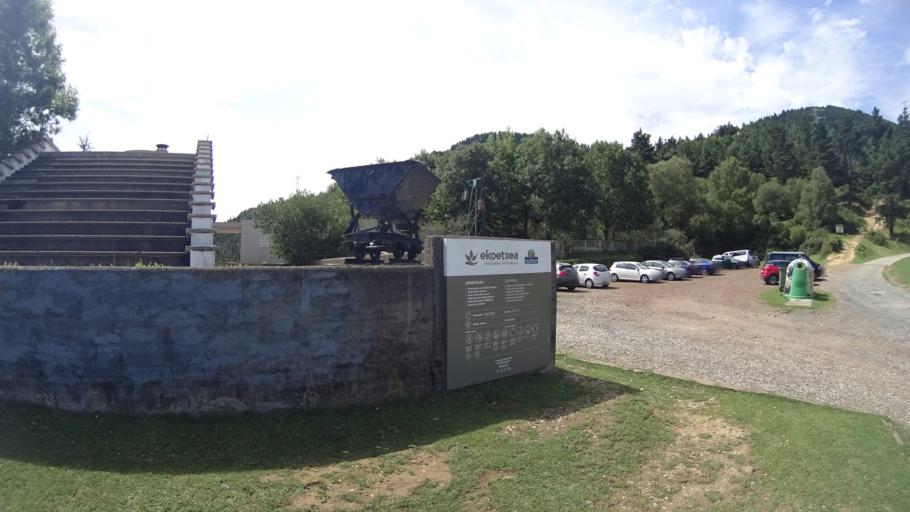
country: ES
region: Basque Country
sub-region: Bizkaia
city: Urtuella
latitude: 43.2833
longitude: -3.0755
